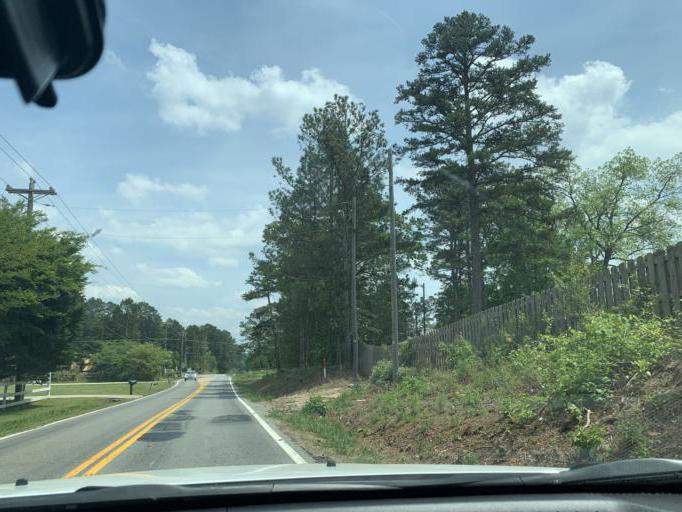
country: US
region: Georgia
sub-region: Forsyth County
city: Cumming
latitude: 34.1496
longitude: -84.1437
